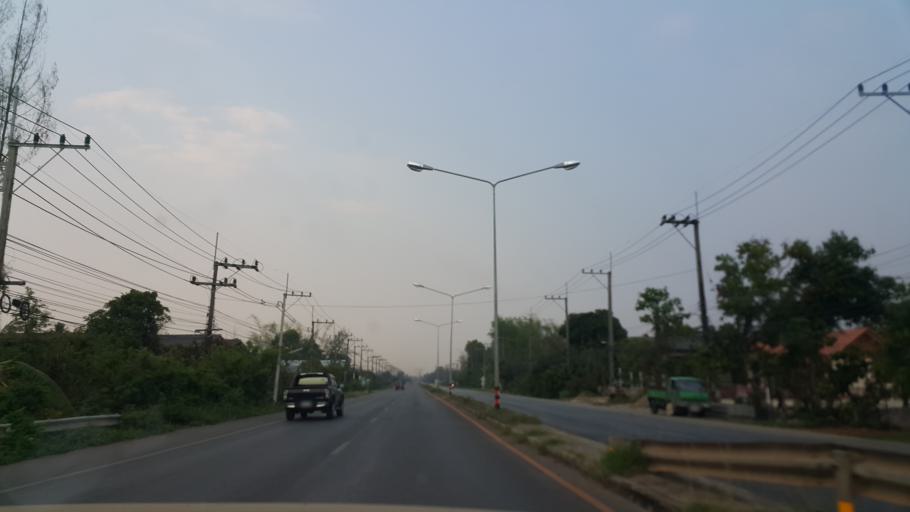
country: TH
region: Nakhon Phanom
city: That Phanom
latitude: 16.9925
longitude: 104.7239
